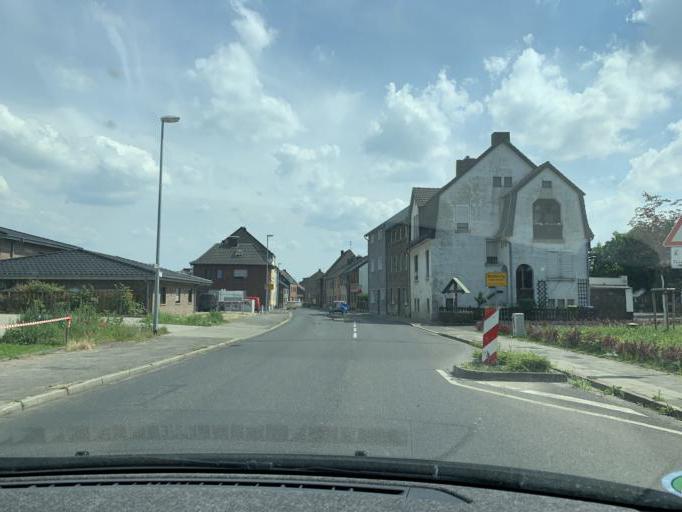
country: DE
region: North Rhine-Westphalia
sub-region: Regierungsbezirk Koln
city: Bedburg
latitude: 50.9853
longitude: 6.5752
